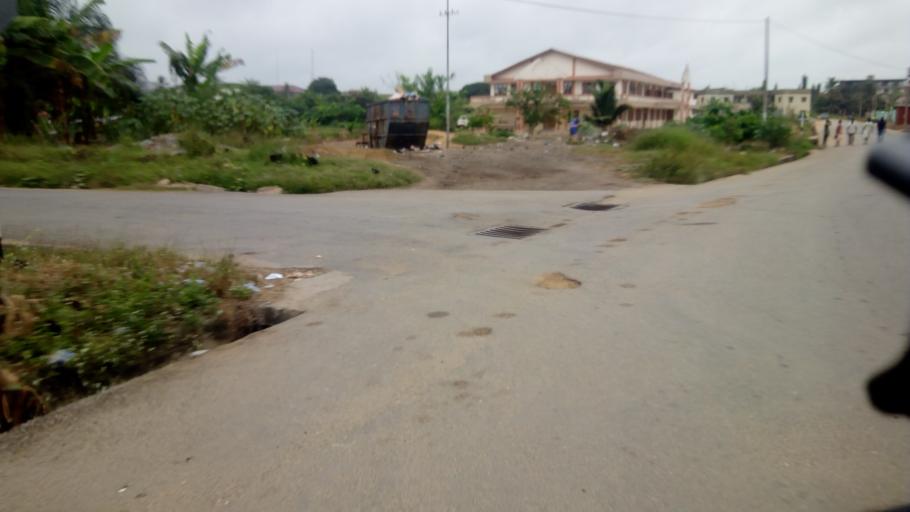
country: GH
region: Central
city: Cape Coast
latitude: 5.1187
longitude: -1.2680
